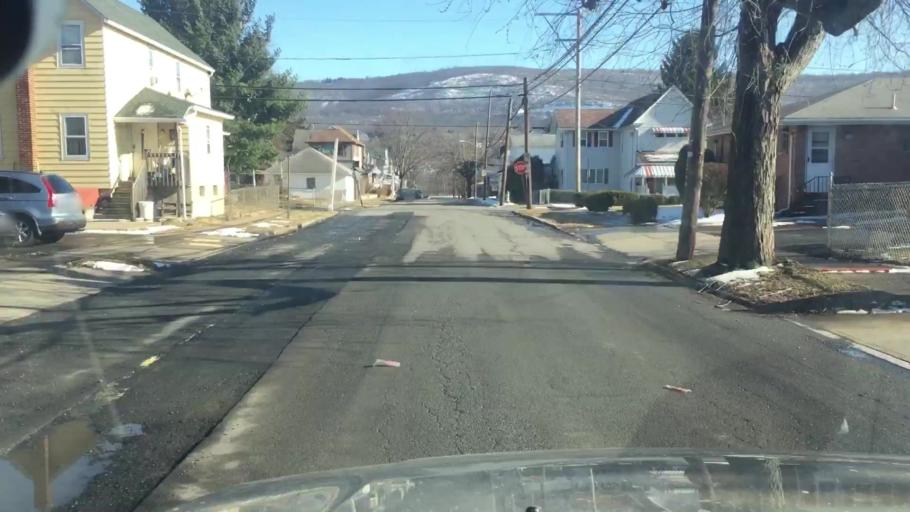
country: US
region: Pennsylvania
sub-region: Luzerne County
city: Wilkes-Barre
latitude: 41.2310
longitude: -75.8845
